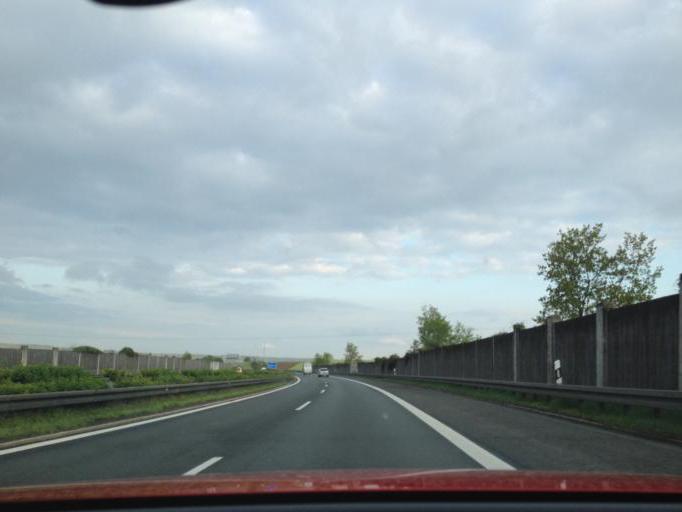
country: DE
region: Bavaria
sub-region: Upper Palatinate
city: Weiden
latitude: 49.6702
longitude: 12.1337
